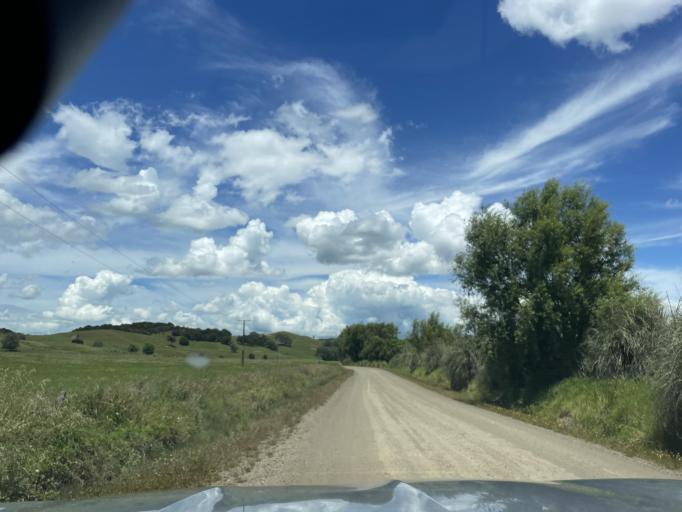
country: NZ
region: Northland
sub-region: Kaipara District
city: Dargaville
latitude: -35.8982
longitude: 173.9172
